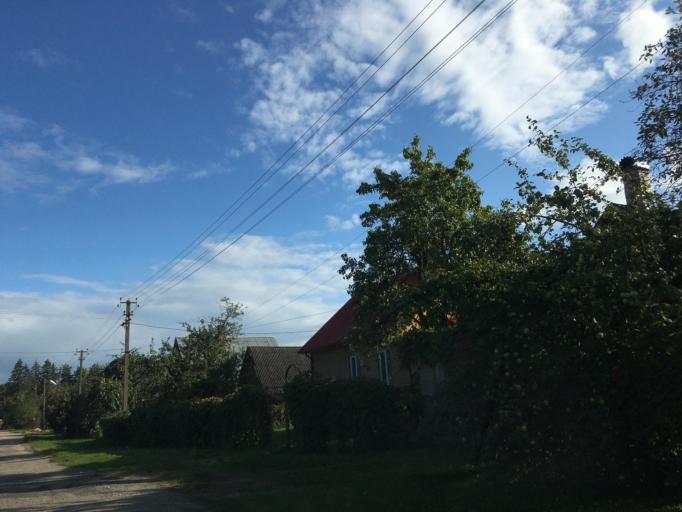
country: RU
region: Pskov
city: Izborsk
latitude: 57.7709
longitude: 27.9730
